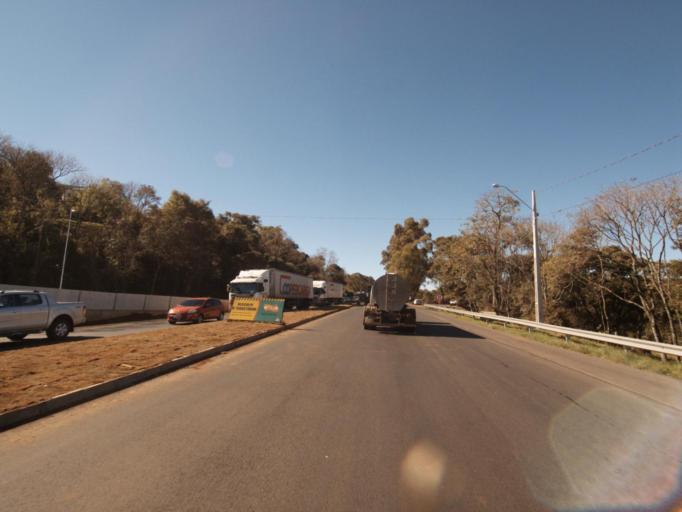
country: BR
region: Santa Catarina
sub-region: Chapeco
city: Chapeco
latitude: -26.9989
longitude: -52.6449
